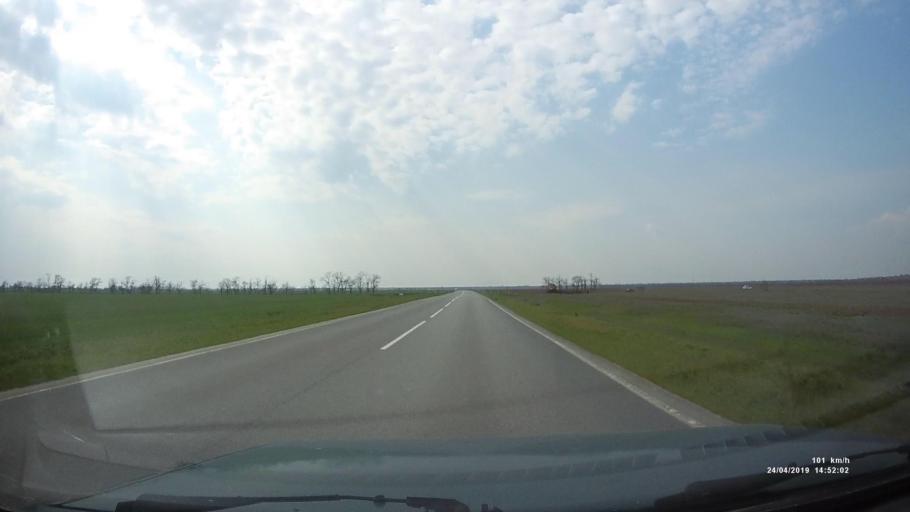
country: RU
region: Rostov
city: Remontnoye
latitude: 46.5290
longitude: 43.6890
